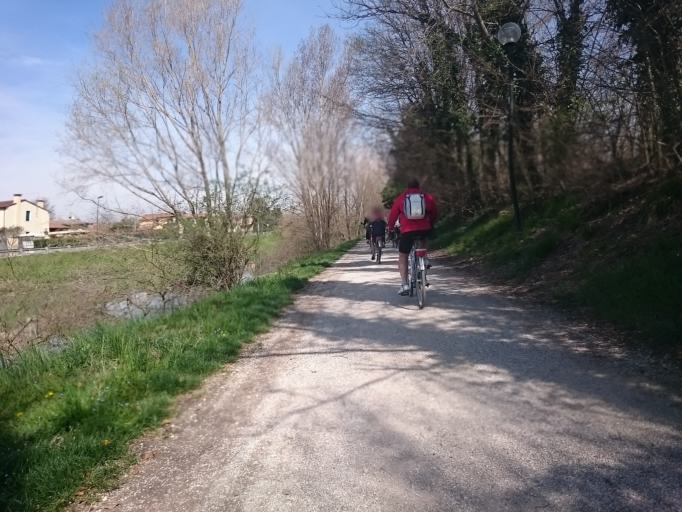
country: IT
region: Veneto
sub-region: Provincia di Padova
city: Taggi
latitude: 45.4564
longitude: 11.8331
